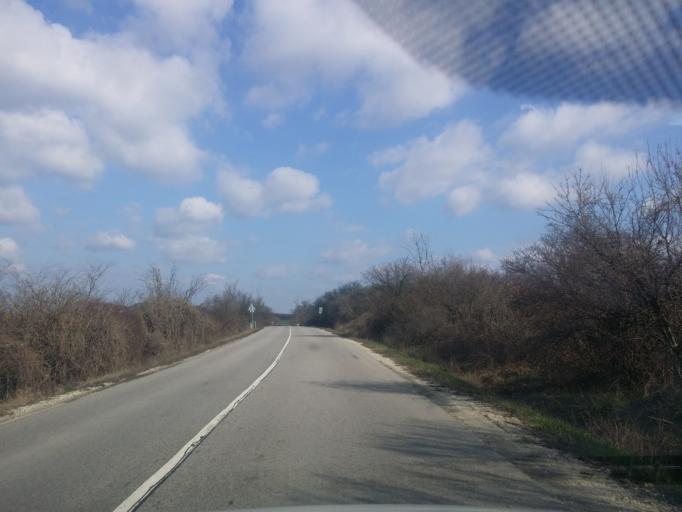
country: HU
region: Pest
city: Zsambek
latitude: 47.5606
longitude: 18.6930
